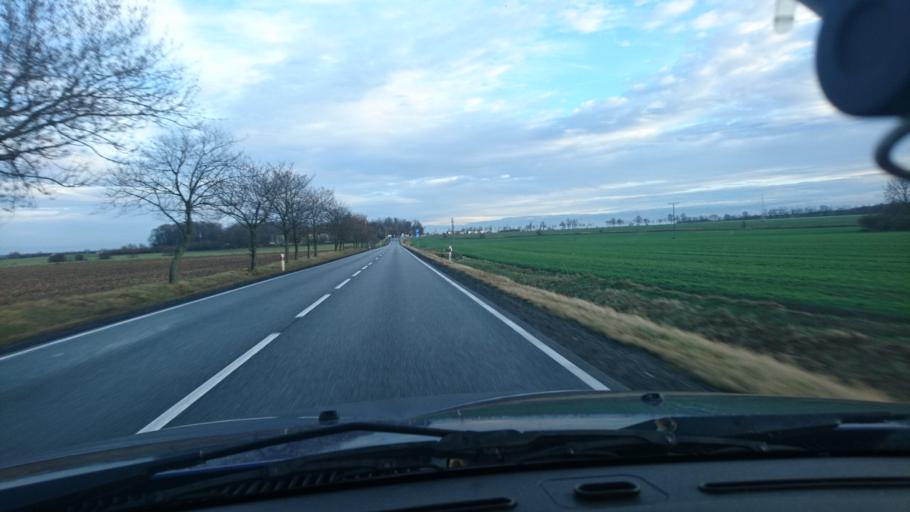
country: PL
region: Greater Poland Voivodeship
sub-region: Powiat kepinski
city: Slupia pod Kepnem
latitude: 51.2441
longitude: 18.0244
